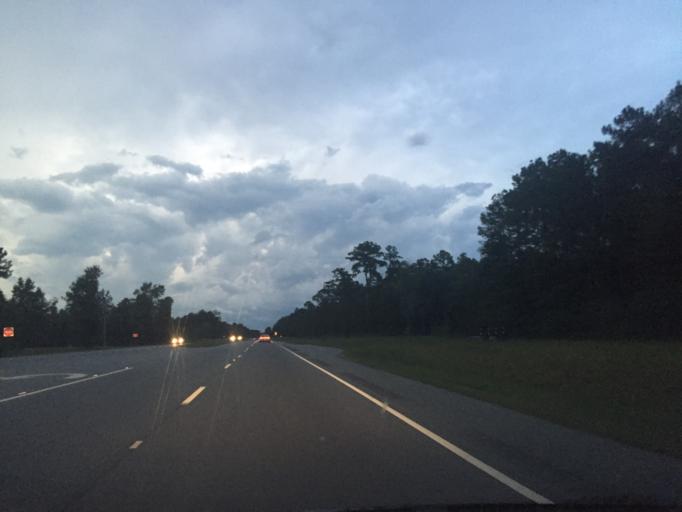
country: US
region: Georgia
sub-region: Liberty County
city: Midway
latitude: 31.8370
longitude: -81.4813
